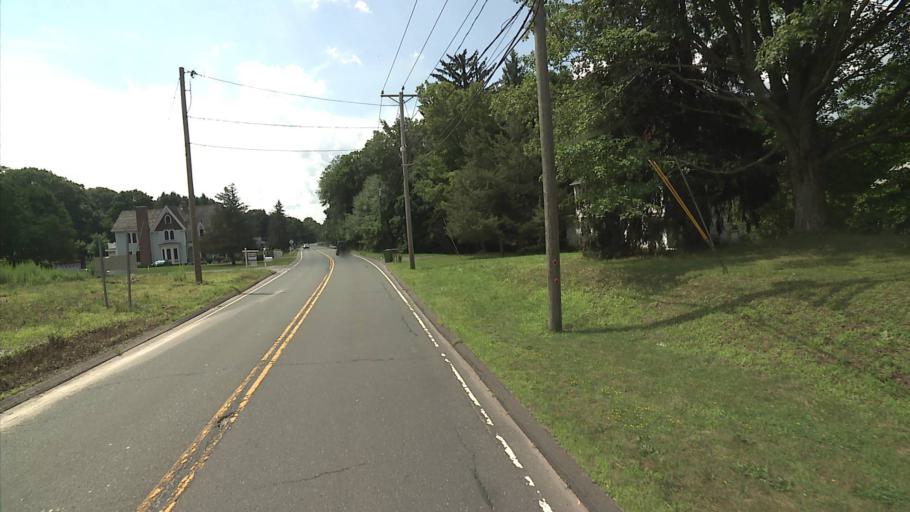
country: US
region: Connecticut
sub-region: Middlesex County
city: Cromwell
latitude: 41.6402
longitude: -72.6060
